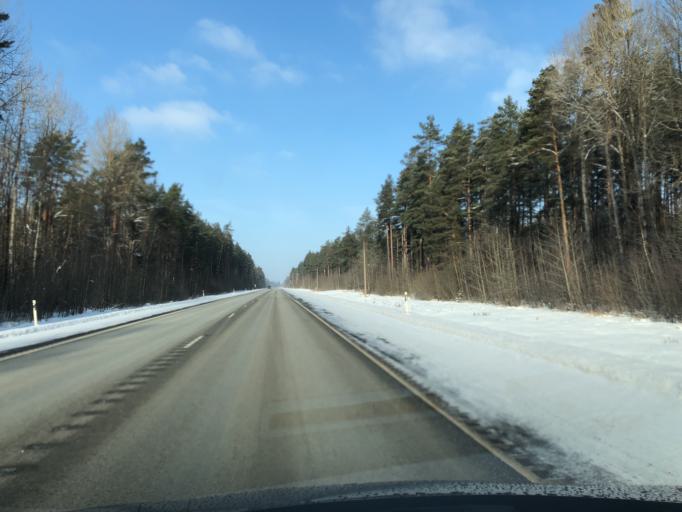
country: EE
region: Tartu
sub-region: Tartu linn
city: Tartu
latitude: 58.3920
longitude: 26.6649
